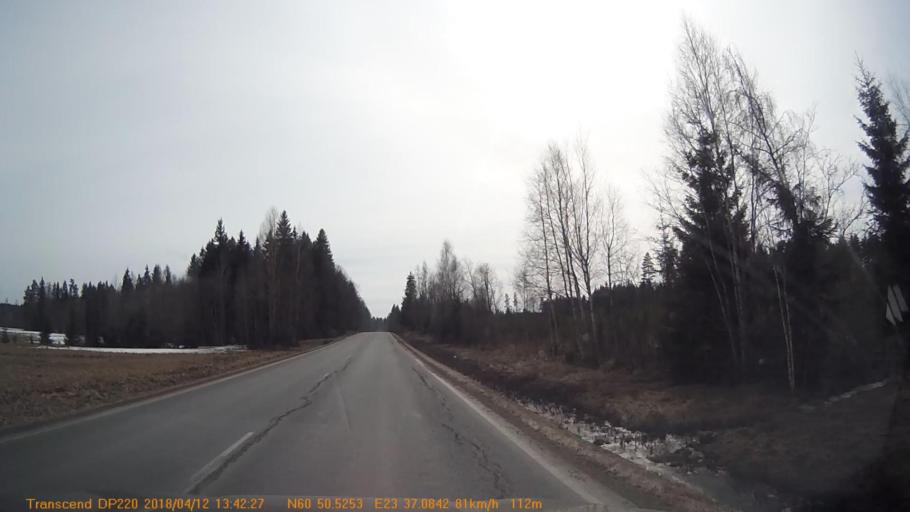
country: FI
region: Haeme
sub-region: Forssa
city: Forssa
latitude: 60.8413
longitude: 23.6181
